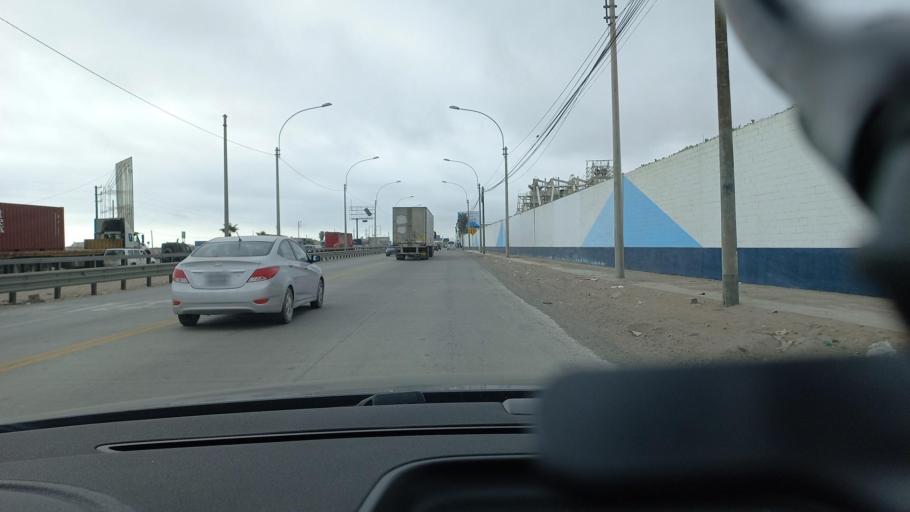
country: PE
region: Lima
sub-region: Lima
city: Surco
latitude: -12.2400
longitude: -76.9480
